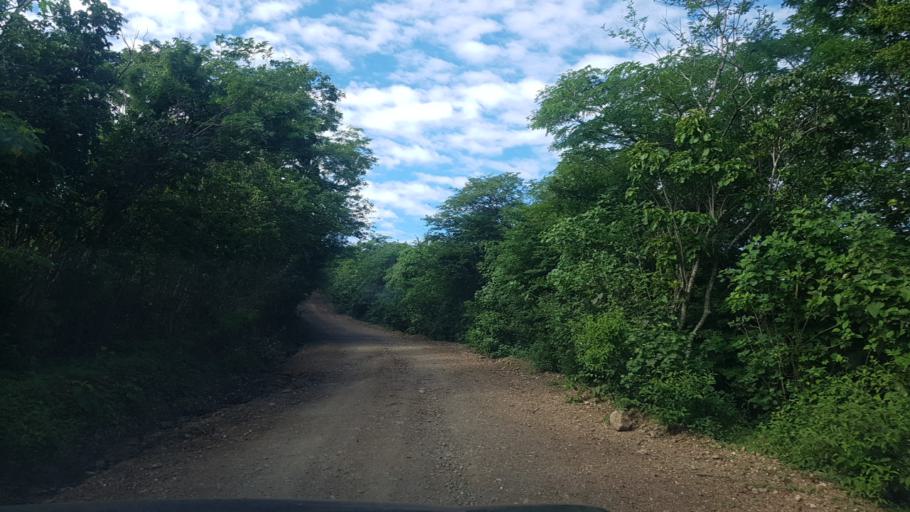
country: NI
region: Nueva Segovia
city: Ocotal
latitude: 13.6001
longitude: -86.4419
